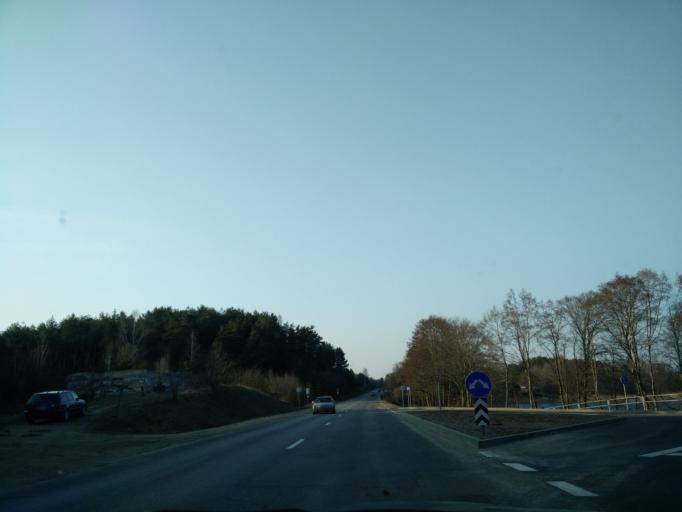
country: LT
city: Trakai
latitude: 54.6547
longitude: 24.9173
